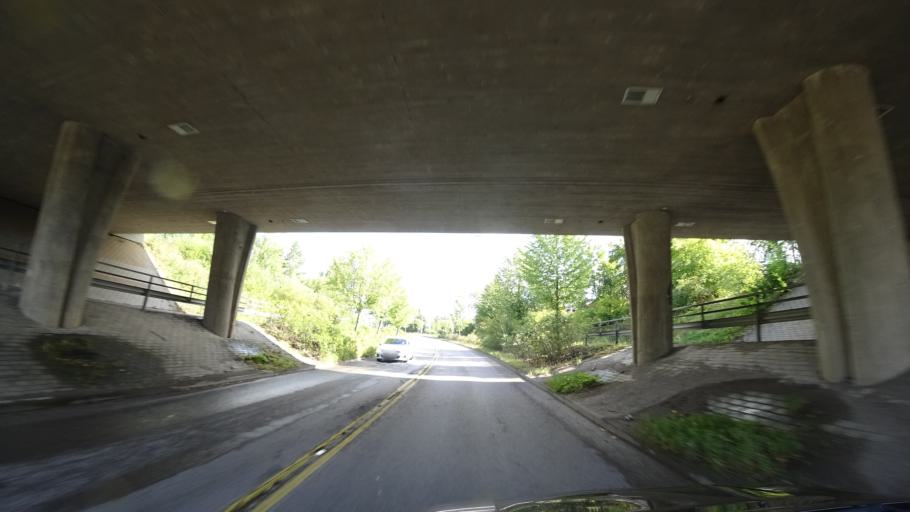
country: FI
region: Uusimaa
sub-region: Helsinki
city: Hyvinge
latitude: 60.5544
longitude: 24.9673
